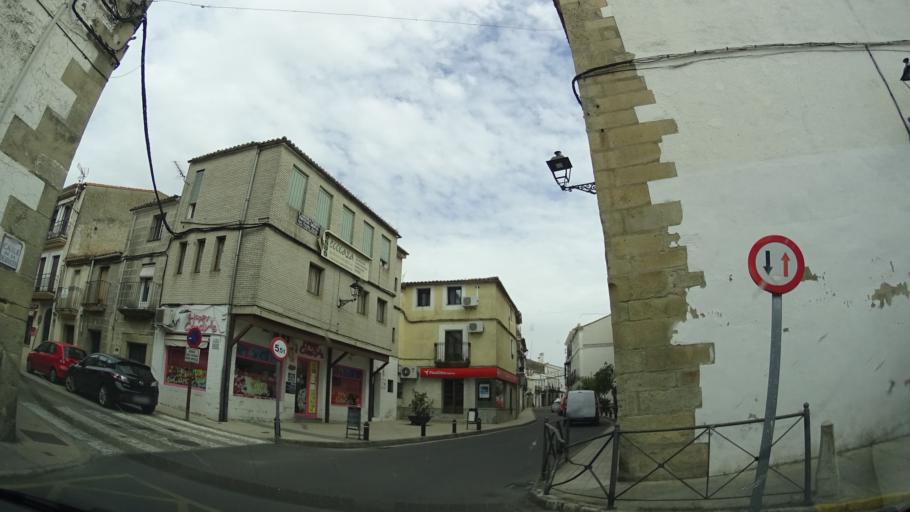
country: ES
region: Extremadura
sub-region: Provincia de Caceres
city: Trujillo
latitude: 39.4578
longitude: -5.8797
